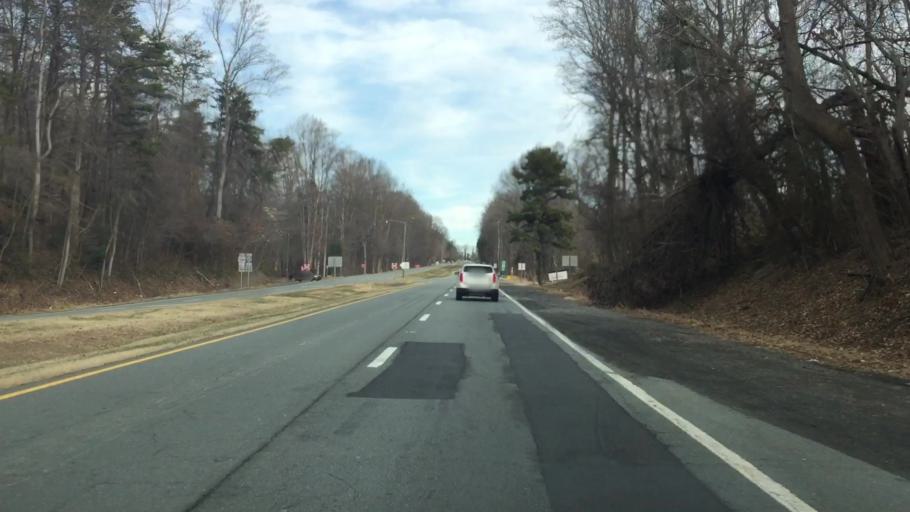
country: US
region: North Carolina
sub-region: Forsyth County
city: Winston-Salem
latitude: 36.1029
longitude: -80.1931
